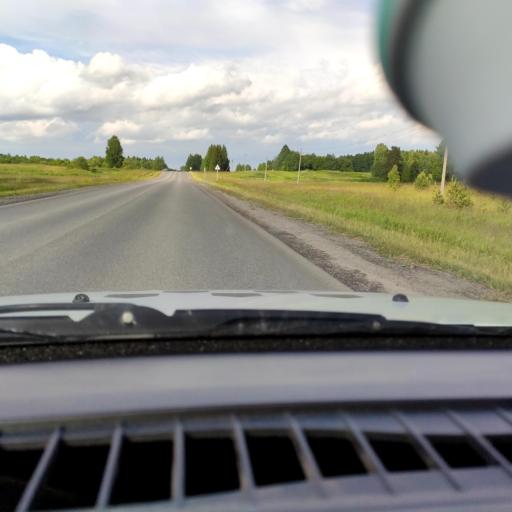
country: RU
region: Perm
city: Orda
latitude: 57.2425
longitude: 56.9875
